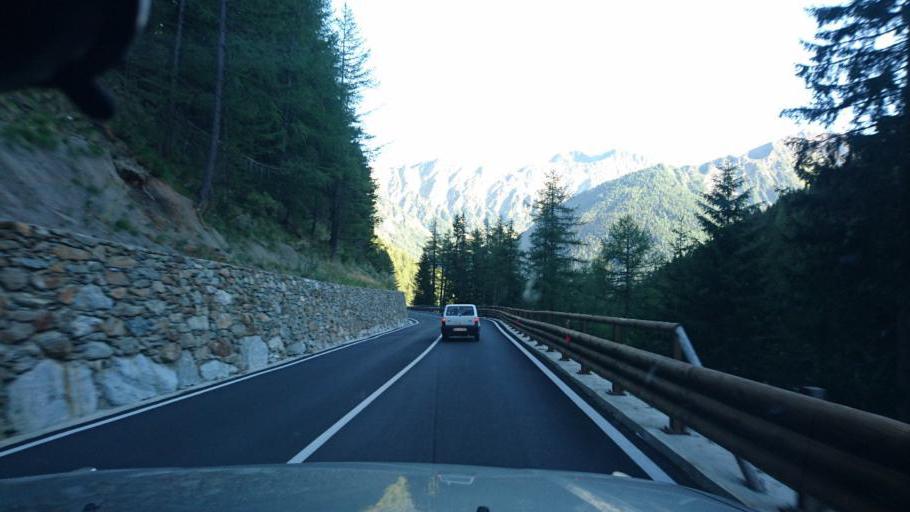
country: IT
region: Aosta Valley
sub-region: Valle d'Aosta
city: San Leonardo
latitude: 45.8368
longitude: 7.1840
